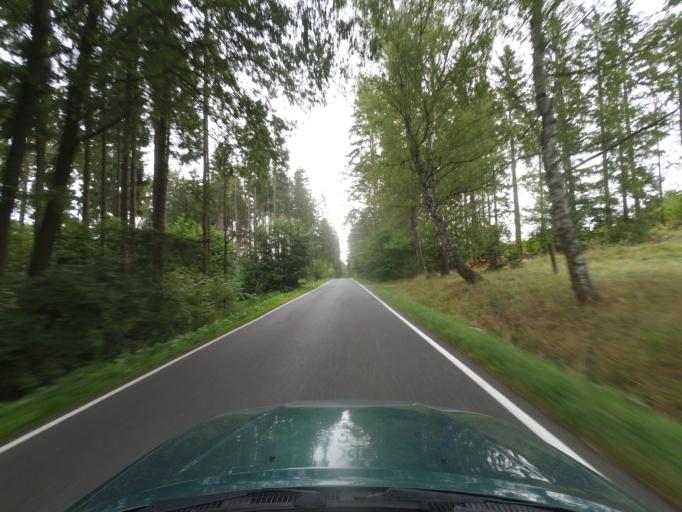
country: CZ
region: Plzensky
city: Bela nad Radbuzou
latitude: 49.5899
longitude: 12.6770
